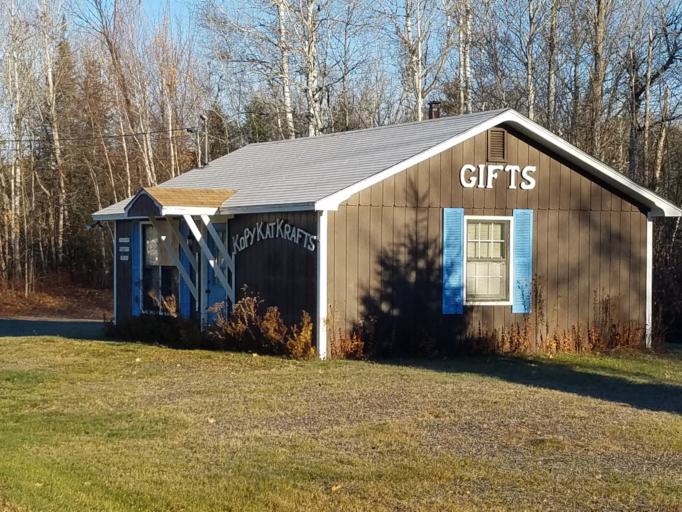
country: US
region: Maine
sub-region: Waldo County
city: Troy
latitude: 44.6512
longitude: -69.2875
